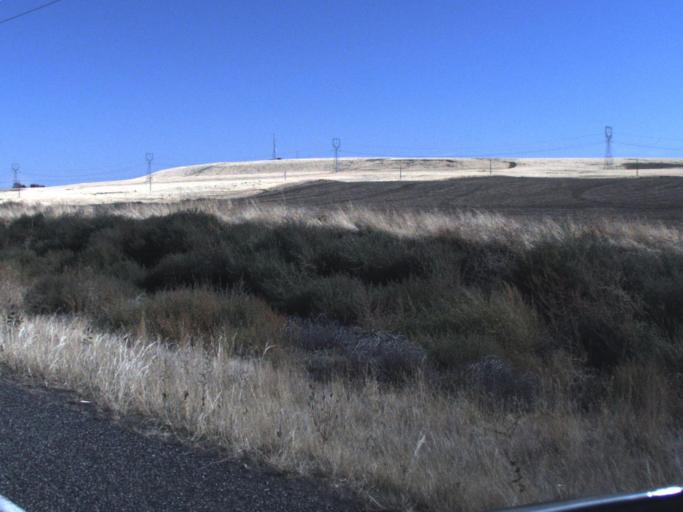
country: US
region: Washington
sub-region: Walla Walla County
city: Burbank
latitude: 46.2927
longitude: -118.7298
